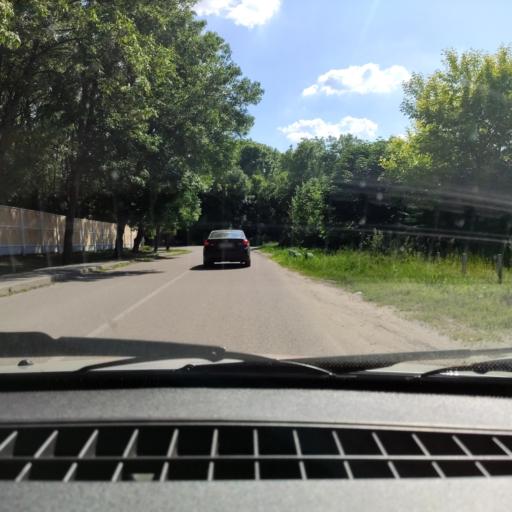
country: RU
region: Voronezj
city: Ramon'
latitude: 51.8246
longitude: 39.2615
